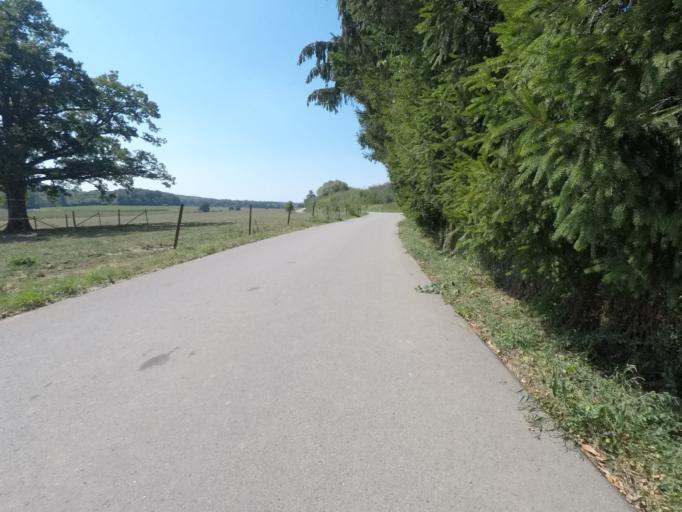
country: LU
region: Luxembourg
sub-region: Canton de Capellen
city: Steinfort
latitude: 49.6343
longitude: 5.9132
